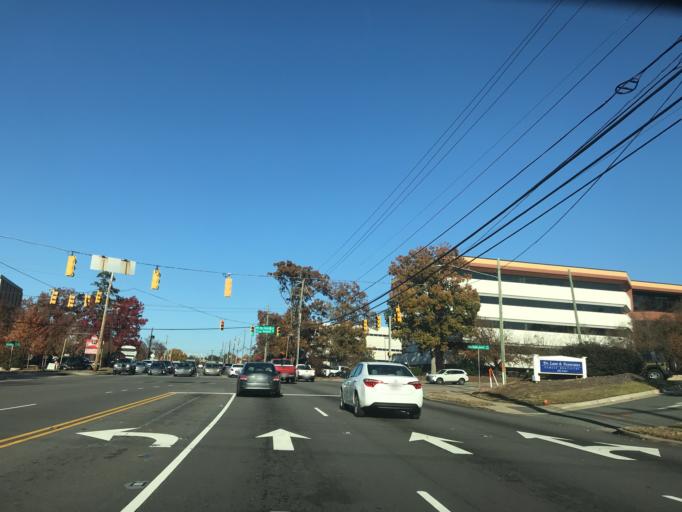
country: US
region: North Carolina
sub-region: Wake County
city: Raleigh
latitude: 35.8367
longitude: -78.6136
